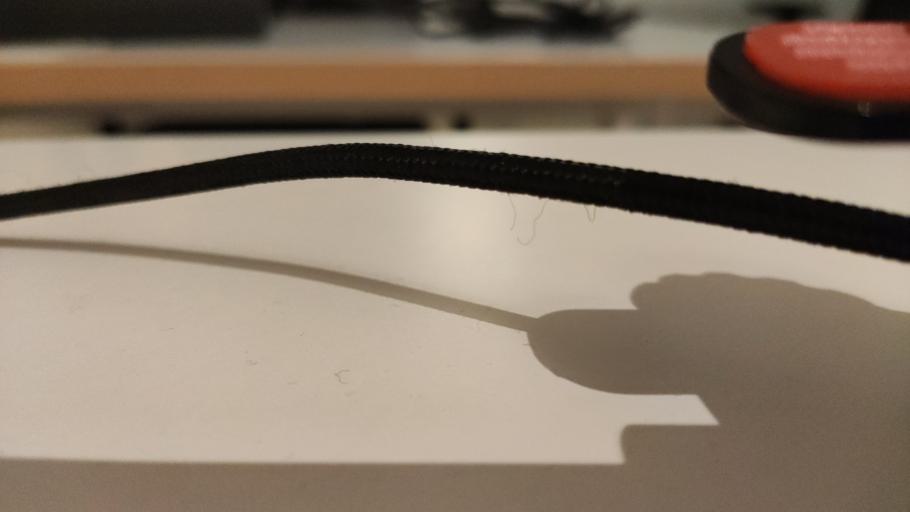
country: RU
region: Moskovskaya
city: Il'inskiy Pogost
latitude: 55.5164
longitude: 38.8716
